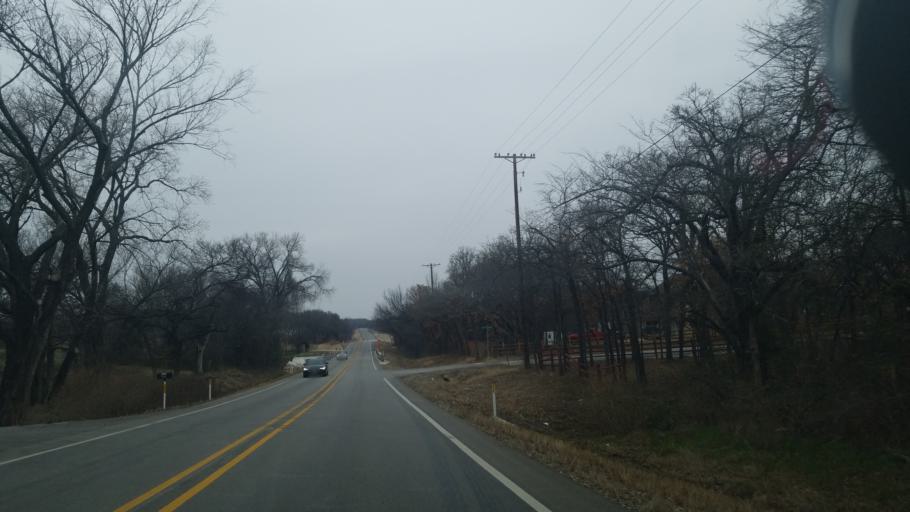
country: US
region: Texas
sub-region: Denton County
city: Argyle
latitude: 33.1197
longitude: -97.1396
